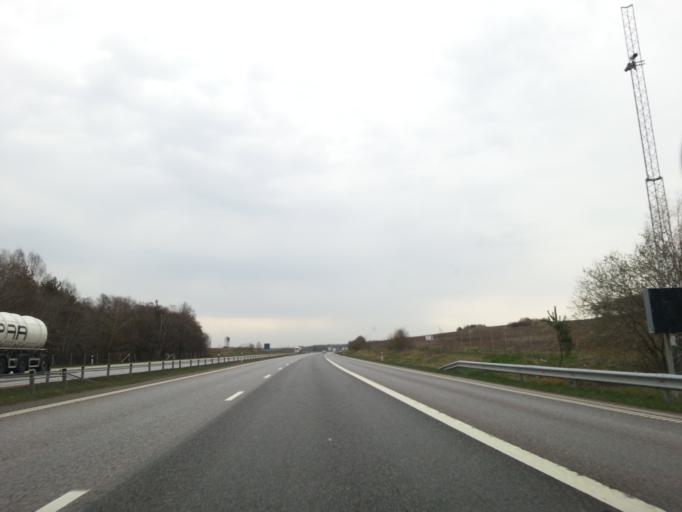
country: SE
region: Halland
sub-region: Halmstads Kommun
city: Halmstad
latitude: 56.7601
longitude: 12.8387
